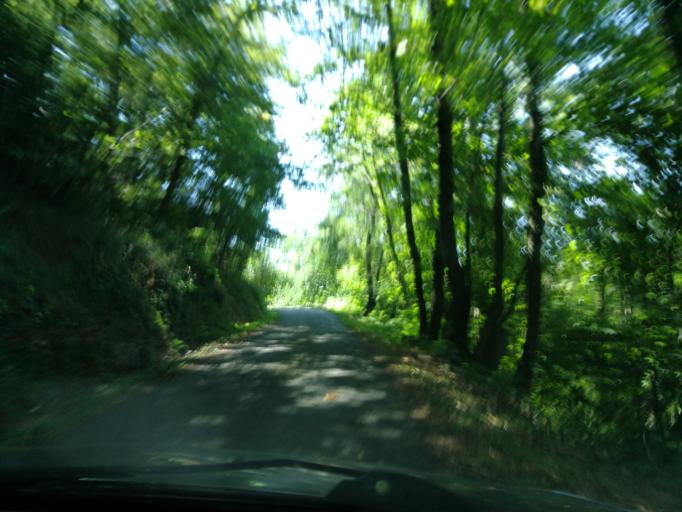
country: FR
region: Midi-Pyrenees
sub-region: Departement de l'Aveyron
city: Livinhac-le-Haut
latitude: 44.6792
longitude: 2.3233
